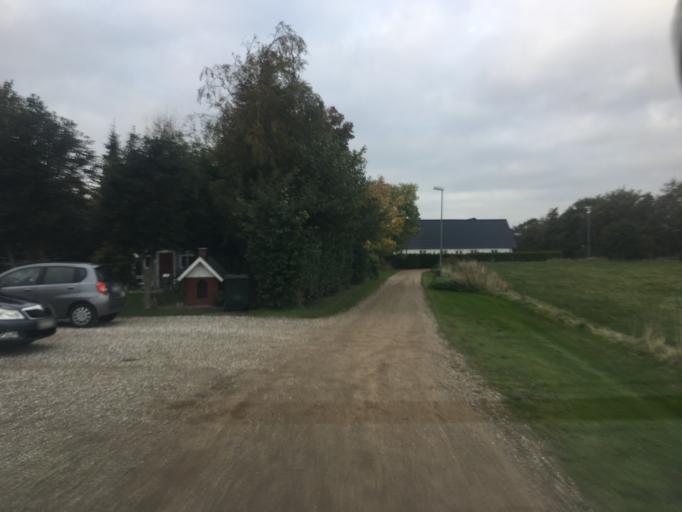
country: DE
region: Schleswig-Holstein
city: Aventoft
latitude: 54.9698
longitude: 8.7703
